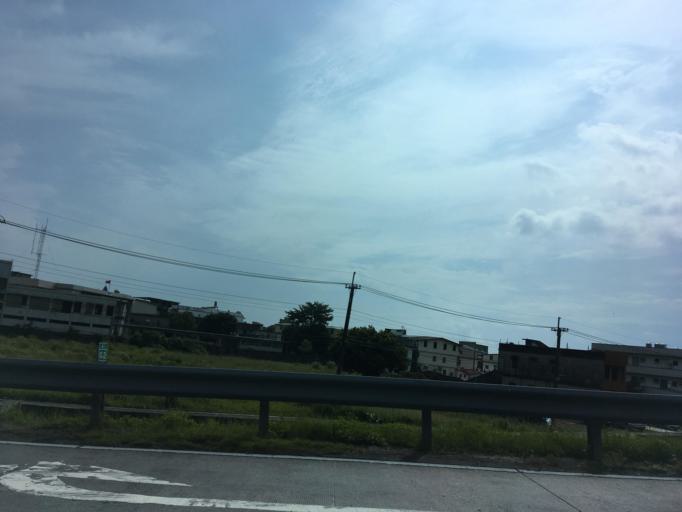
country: TW
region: Taiwan
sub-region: Yilan
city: Yilan
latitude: 24.8374
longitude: 121.7912
